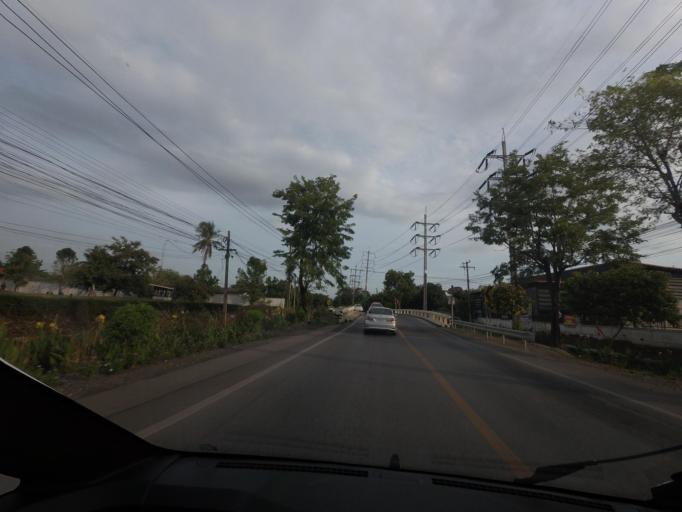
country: TH
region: Bangkok
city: Nong Chok
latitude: 13.8861
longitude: 100.8636
